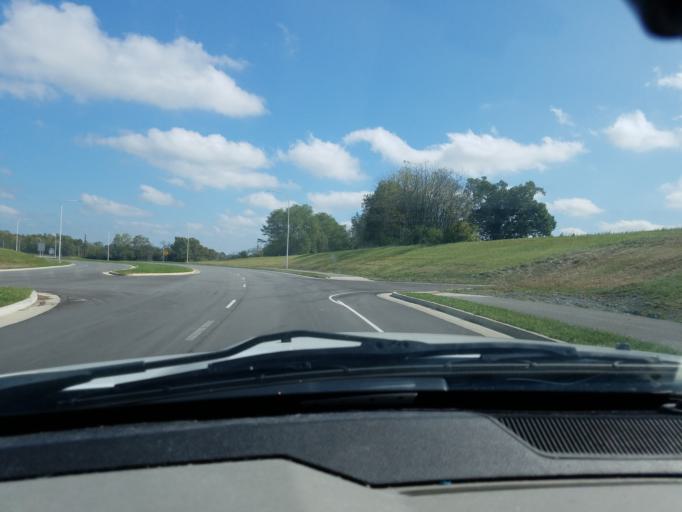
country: US
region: Kentucky
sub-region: Scott County
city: Georgetown
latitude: 38.2430
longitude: -84.5393
